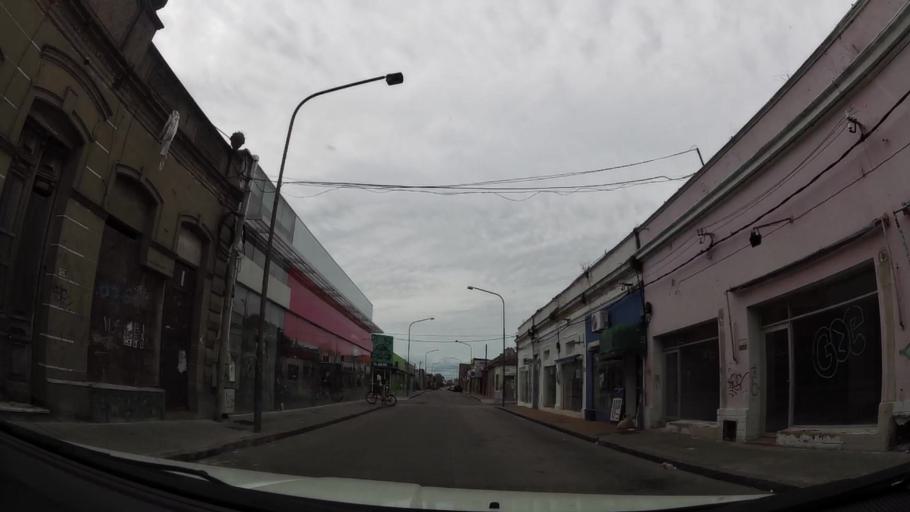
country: UY
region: Maldonado
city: Maldonado
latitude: -34.9049
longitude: -54.9577
